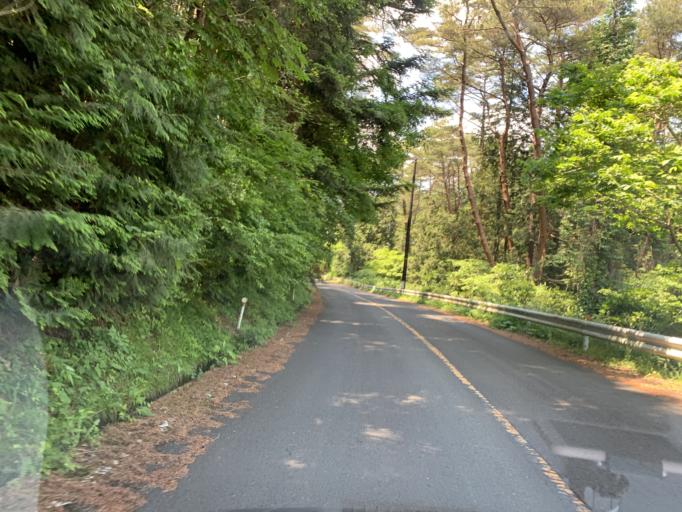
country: JP
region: Miyagi
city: Matsushima
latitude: 38.3585
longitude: 141.0569
